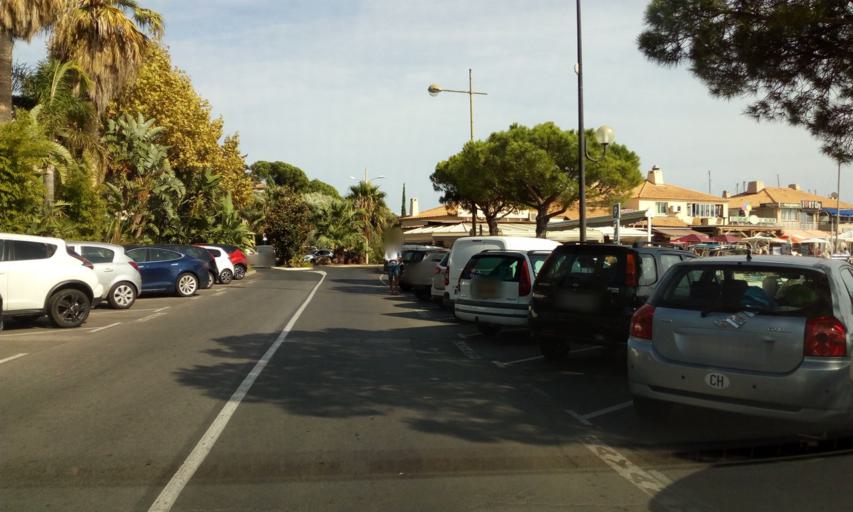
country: FR
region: Provence-Alpes-Cote d'Azur
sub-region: Departement du Var
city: Le Lavandou
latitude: 43.1379
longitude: 6.3730
